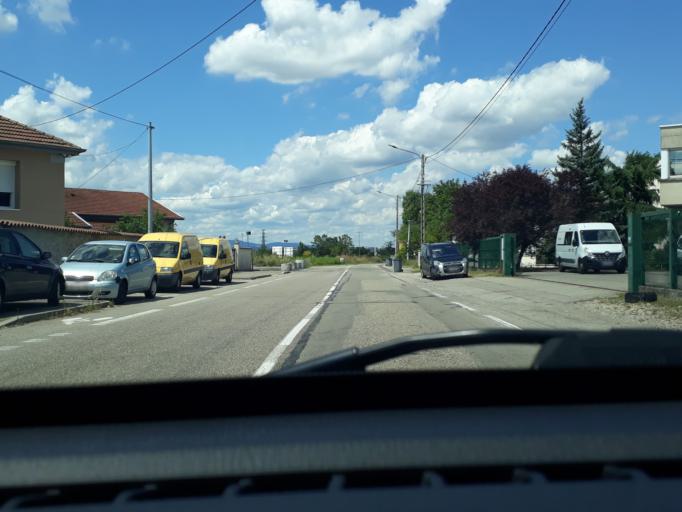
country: FR
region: Rhone-Alpes
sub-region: Departement du Rhone
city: Saint-Priest
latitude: 45.7109
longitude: 4.9232
